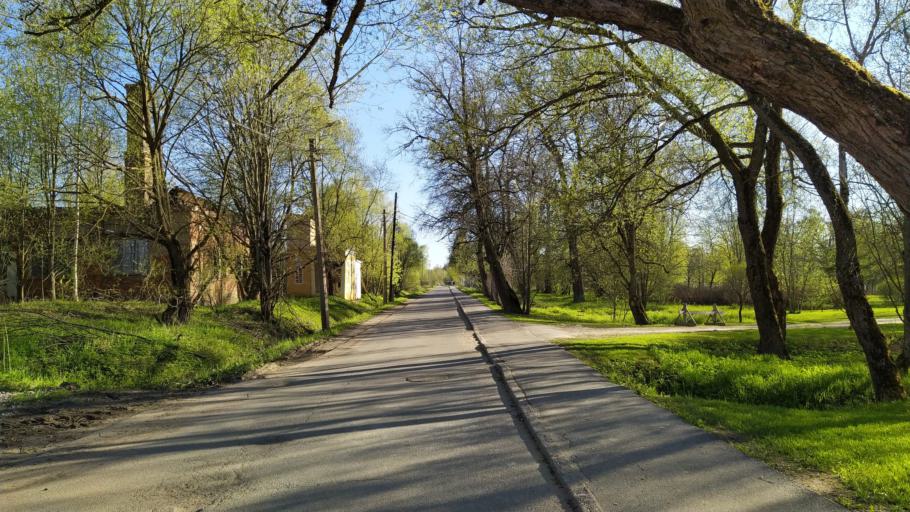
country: RU
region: St.-Petersburg
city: Pavlovsk
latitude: 59.6778
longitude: 30.4479
